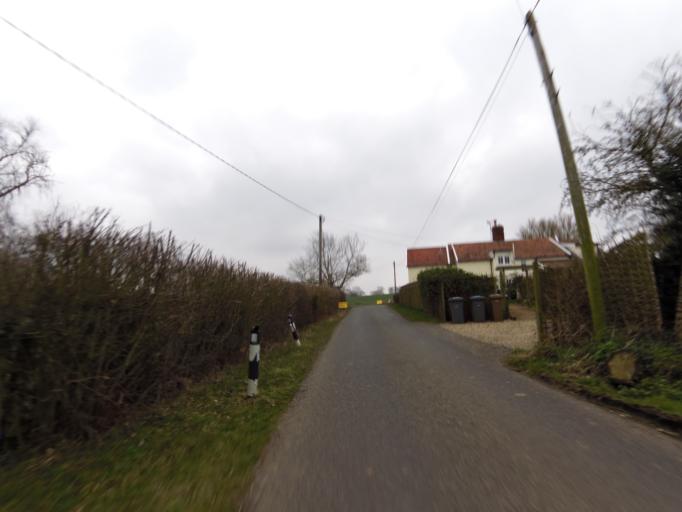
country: GB
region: England
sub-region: Suffolk
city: Framlingham
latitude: 52.2081
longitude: 1.3310
